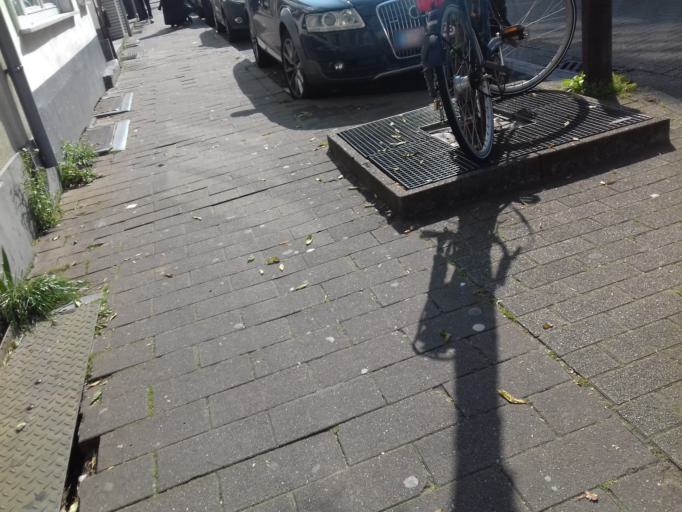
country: BE
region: Flanders
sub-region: Provincie Antwerpen
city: Antwerpen
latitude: 51.2267
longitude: 4.4253
